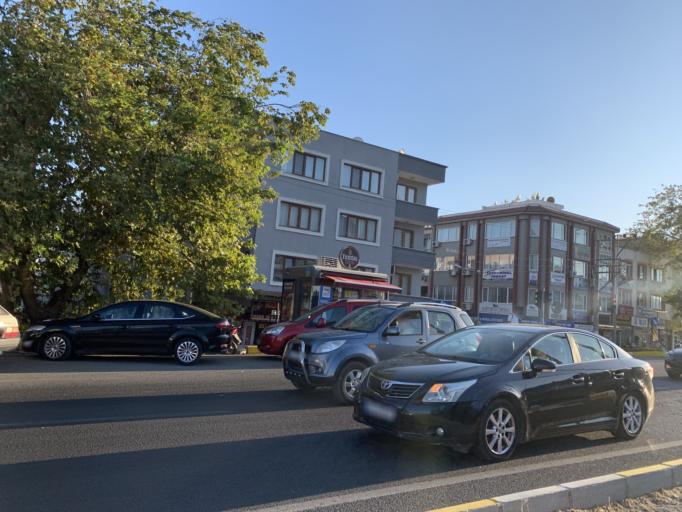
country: TR
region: Balikesir
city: Altinoluk
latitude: 39.5685
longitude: 26.7449
